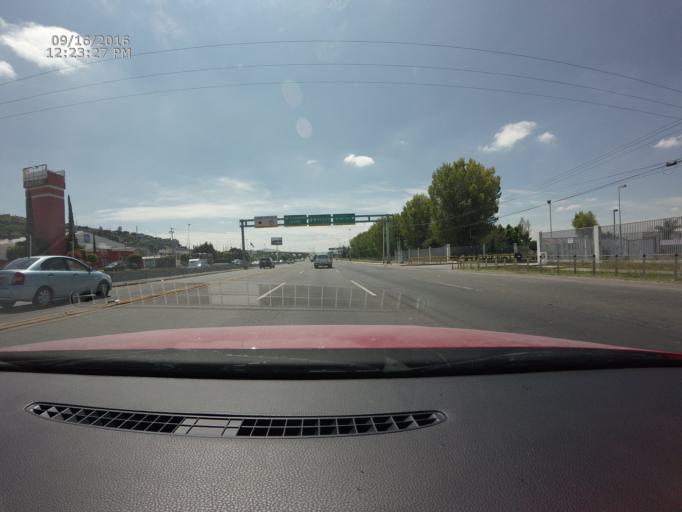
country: MX
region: Queretaro
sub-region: Queretaro
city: Sergio Villasenor
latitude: 20.6269
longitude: -100.4247
